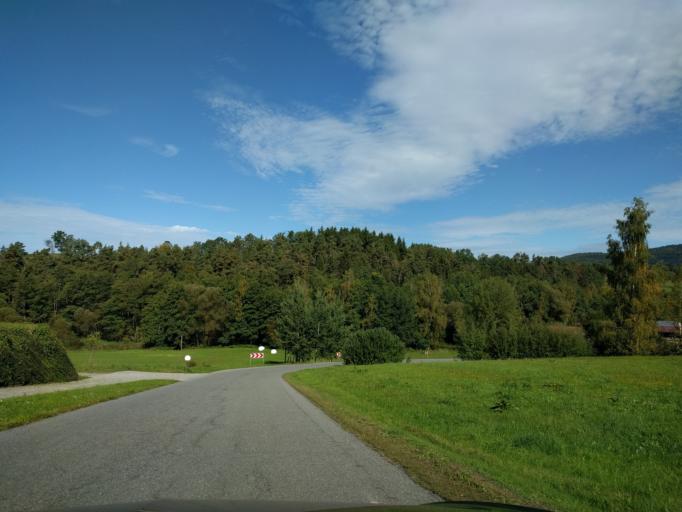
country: DE
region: Bavaria
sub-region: Upper Palatinate
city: Kotzting
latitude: 49.1573
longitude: 12.8867
